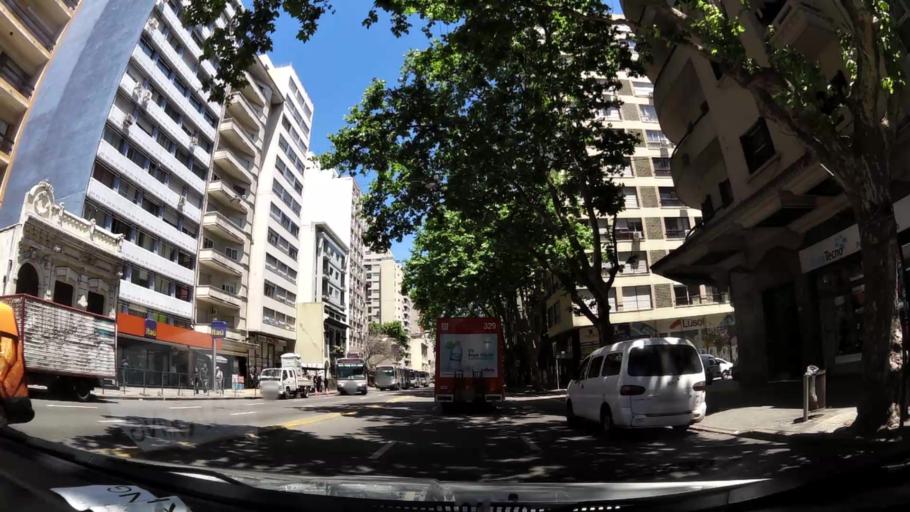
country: UY
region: Montevideo
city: Montevideo
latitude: -34.8987
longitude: -56.1677
